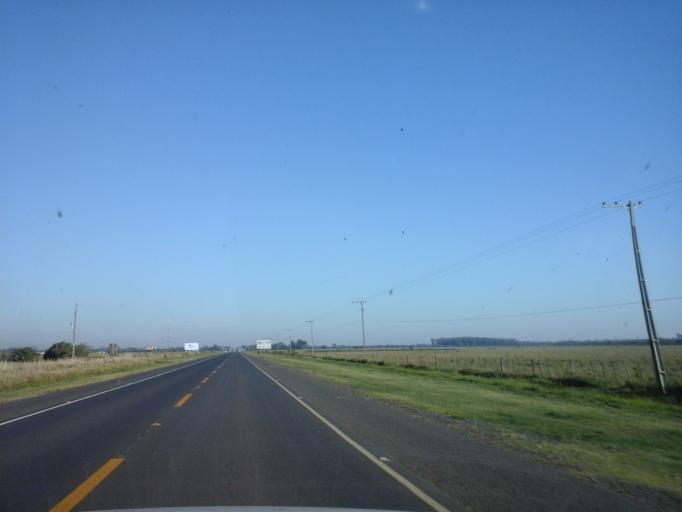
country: PY
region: Neembucu
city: Pilar
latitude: -26.8436
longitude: -58.2662
